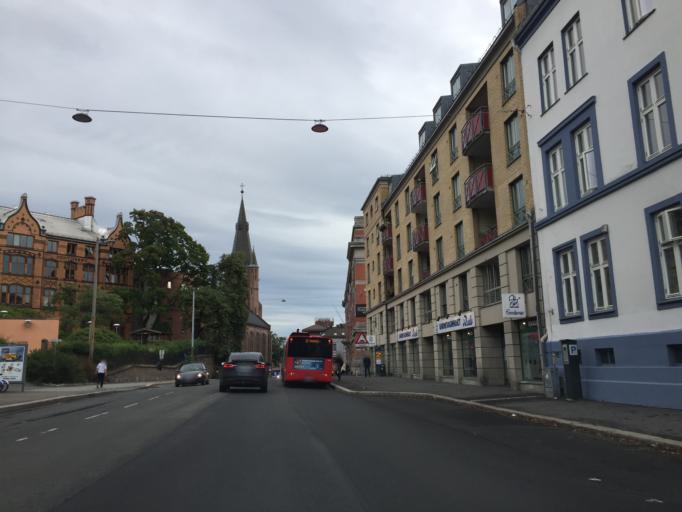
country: NO
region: Oslo
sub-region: Oslo
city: Oslo
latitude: 59.9197
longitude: 10.7435
